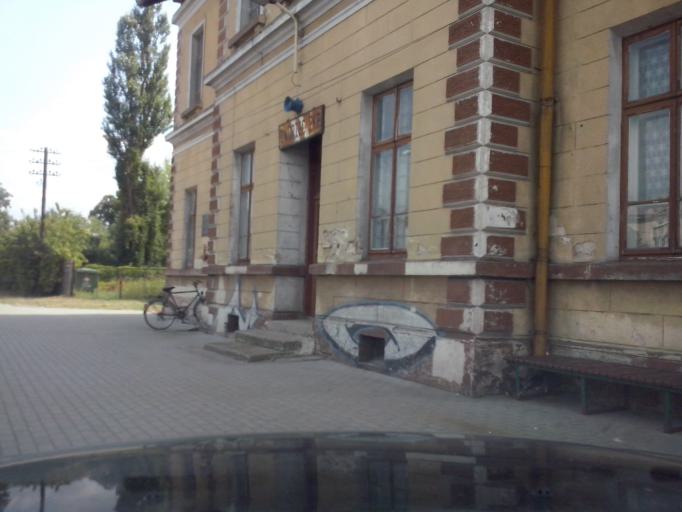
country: PL
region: Subcarpathian Voivodeship
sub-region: Powiat nizanski
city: Nisko
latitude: 50.5137
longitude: 22.1425
